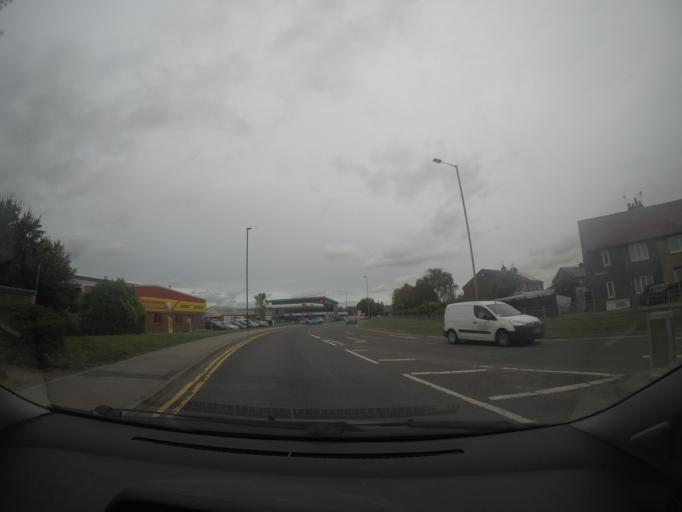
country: GB
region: England
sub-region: North Yorkshire
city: Selby
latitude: 53.7735
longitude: -1.0648
